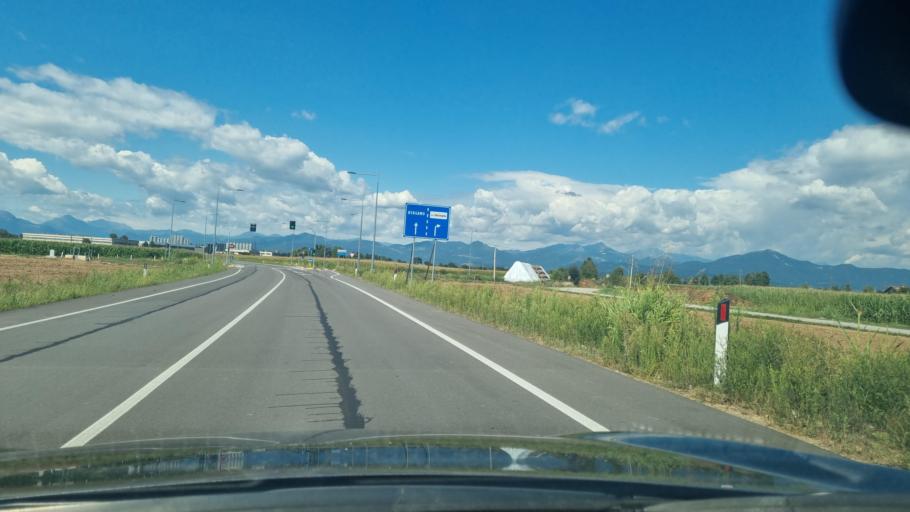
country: IT
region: Lombardy
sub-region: Provincia di Bergamo
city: Ghisalba
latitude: 45.6008
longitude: 9.7692
